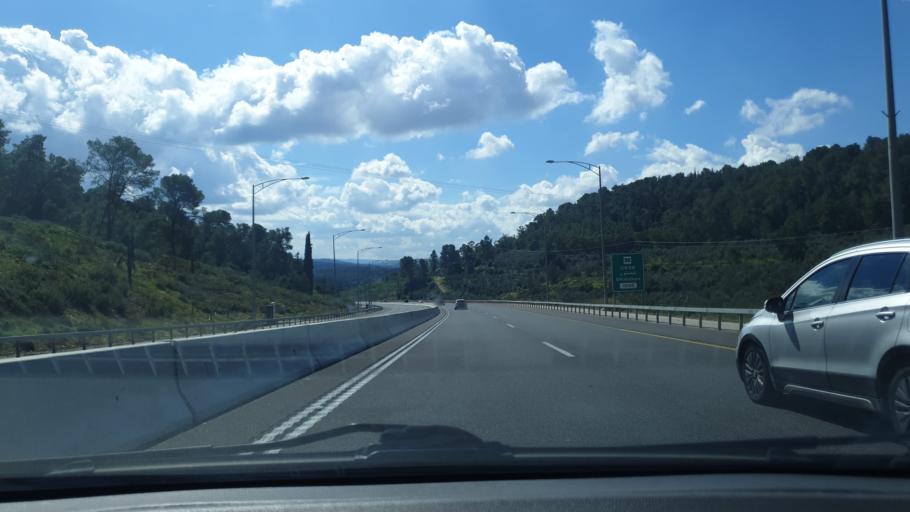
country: IL
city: Mevo horon
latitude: 31.7910
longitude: 35.0140
